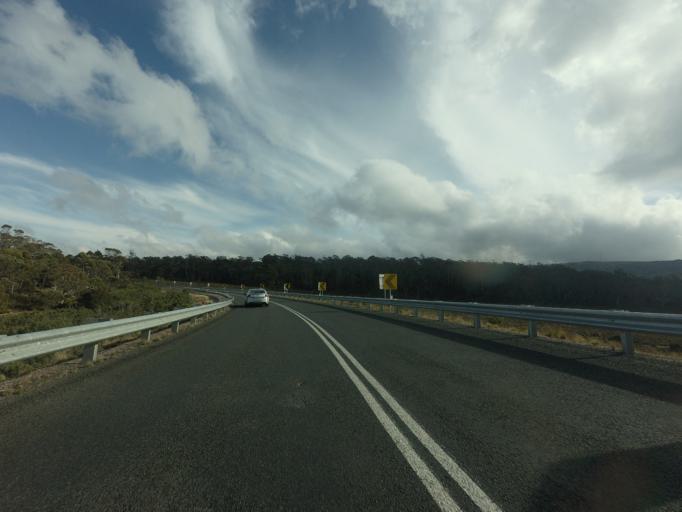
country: AU
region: Tasmania
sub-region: Meander Valley
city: Deloraine
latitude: -41.7864
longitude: 146.6937
